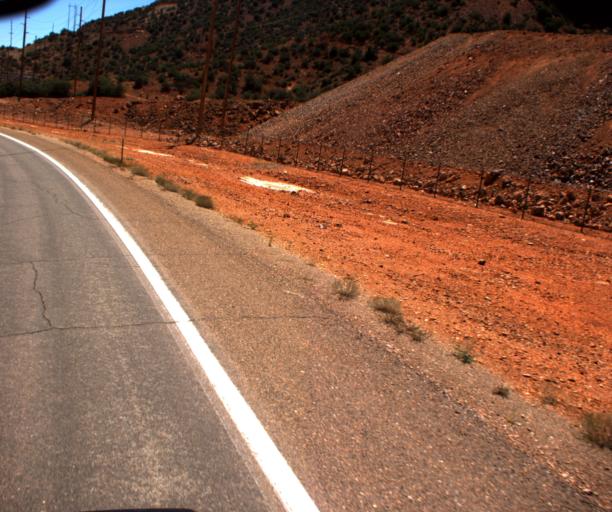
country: US
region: Arizona
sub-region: Greenlee County
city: Morenci
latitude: 33.1003
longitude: -109.3818
